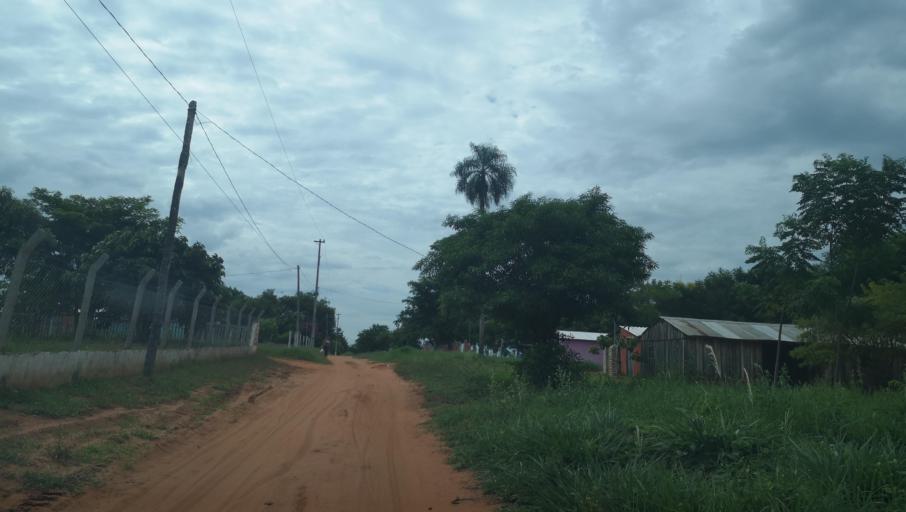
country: PY
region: San Pedro
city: Capiibary
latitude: -24.7191
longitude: -56.0126
